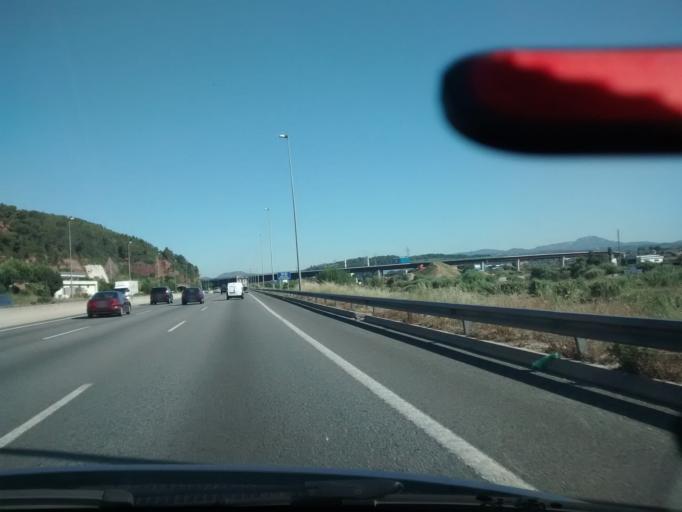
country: ES
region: Catalonia
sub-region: Provincia de Barcelona
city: Palleja
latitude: 41.4321
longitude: 1.9956
